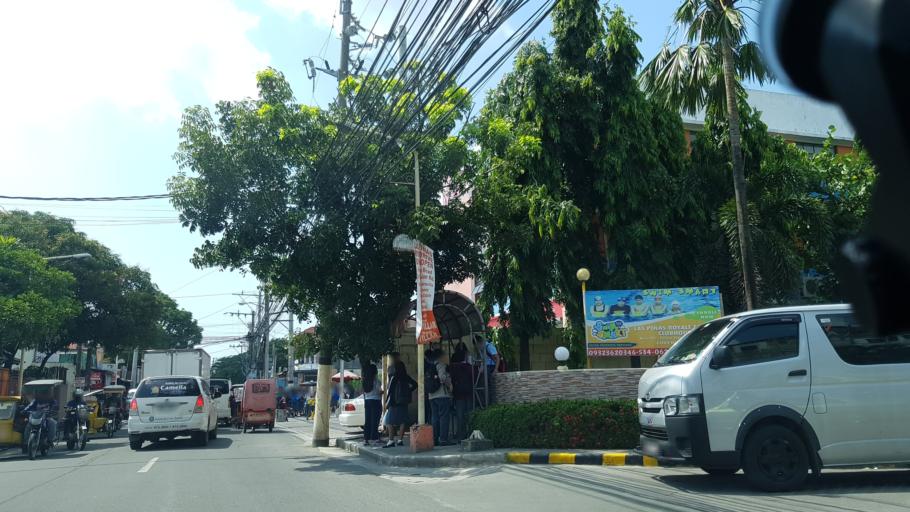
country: PH
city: Sambayanihan People's Village
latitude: 14.4638
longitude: 120.9874
